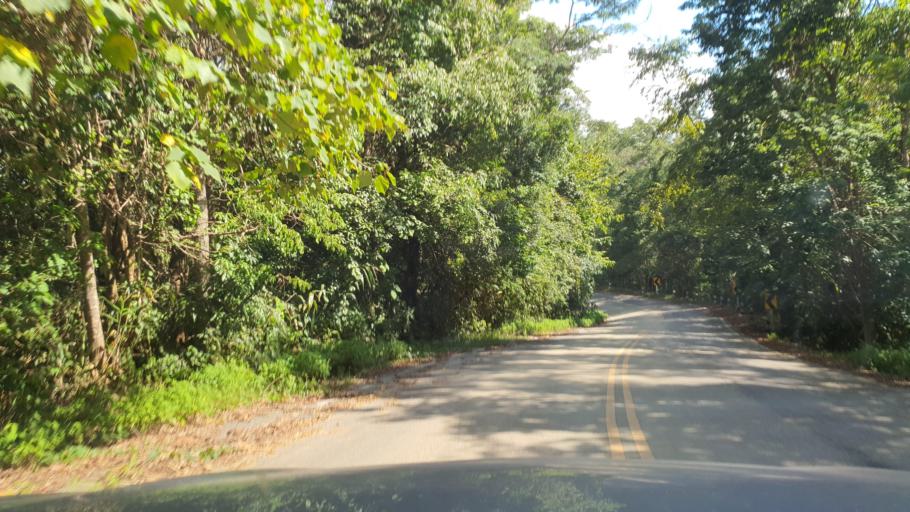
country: TH
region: Chiang Rai
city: Wiang Pa Pao
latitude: 19.3032
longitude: 99.3678
